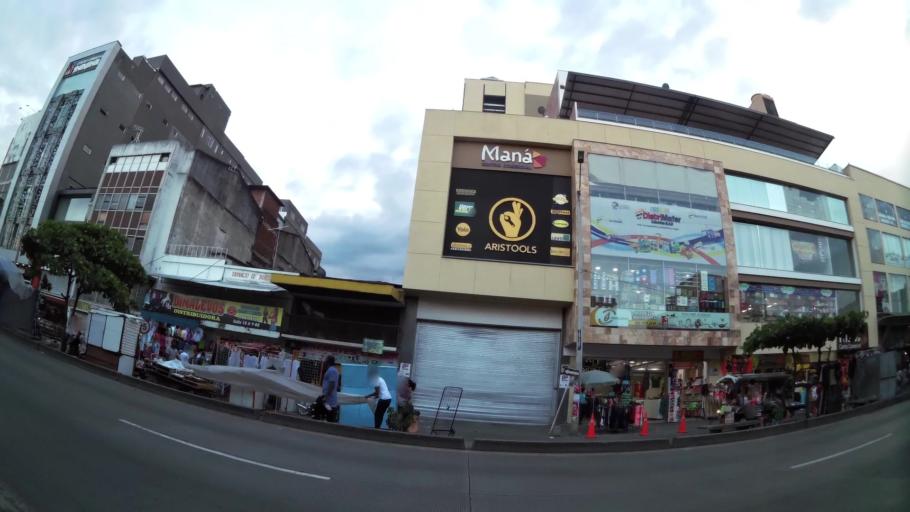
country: CO
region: Valle del Cauca
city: Cali
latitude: 3.4508
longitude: -76.5285
